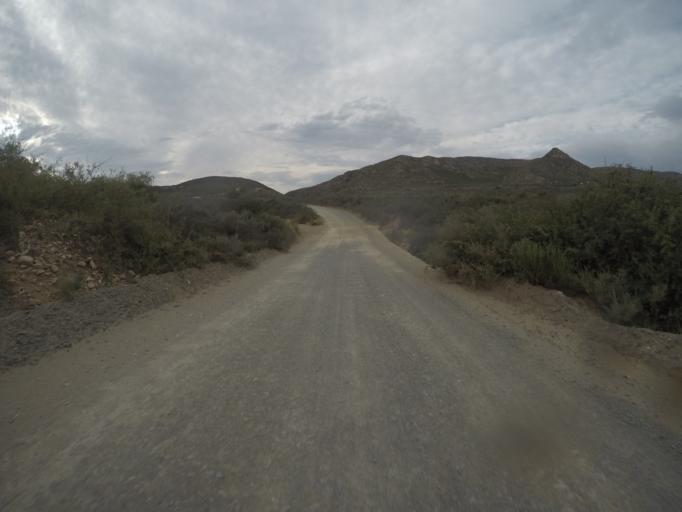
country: ZA
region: Eastern Cape
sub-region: Cacadu District Municipality
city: Willowmore
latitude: -33.4983
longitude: 23.6371
